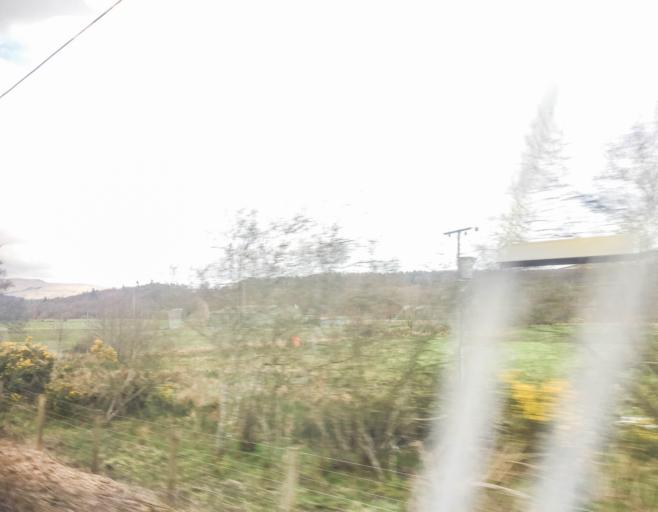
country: GB
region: Scotland
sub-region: Argyll and Bute
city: Helensburgh
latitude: 55.9840
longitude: -4.6925
